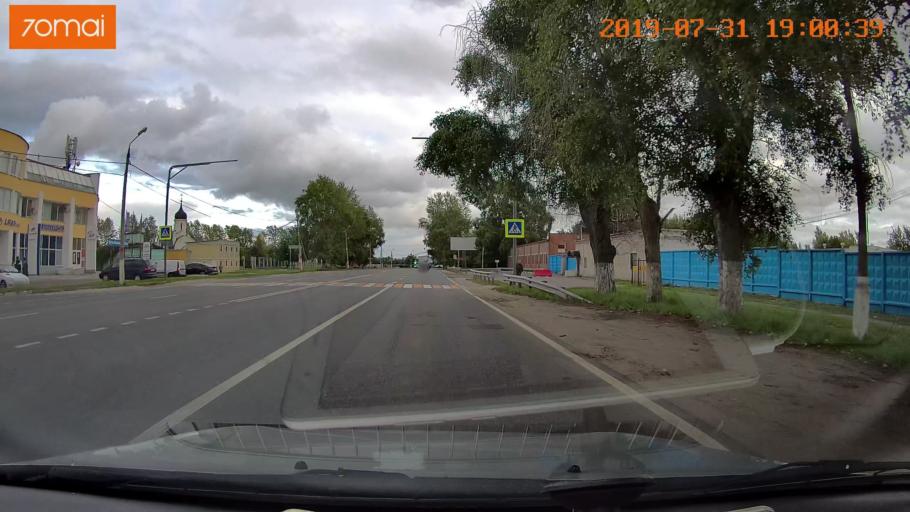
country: RU
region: Moskovskaya
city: Raduzhnyy
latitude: 55.1320
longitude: 38.7258
